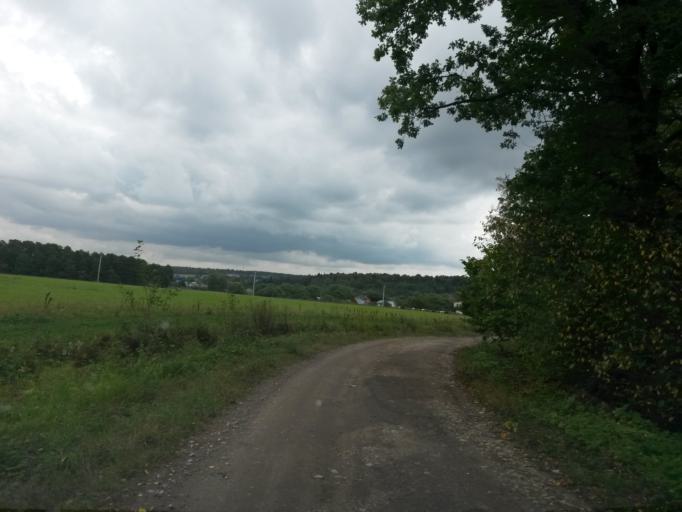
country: RU
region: Moskovskaya
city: Lyubuchany
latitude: 55.2912
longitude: 37.6238
